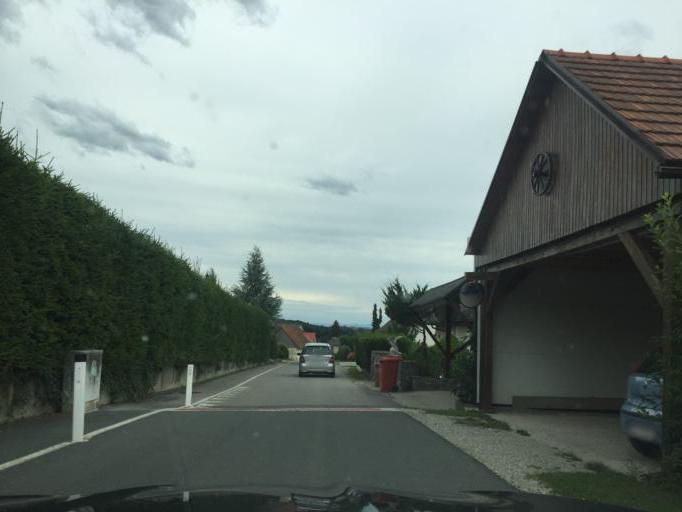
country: AT
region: Styria
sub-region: Politischer Bezirk Graz-Umgebung
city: Hart bei Graz
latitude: 47.0583
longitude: 15.5136
